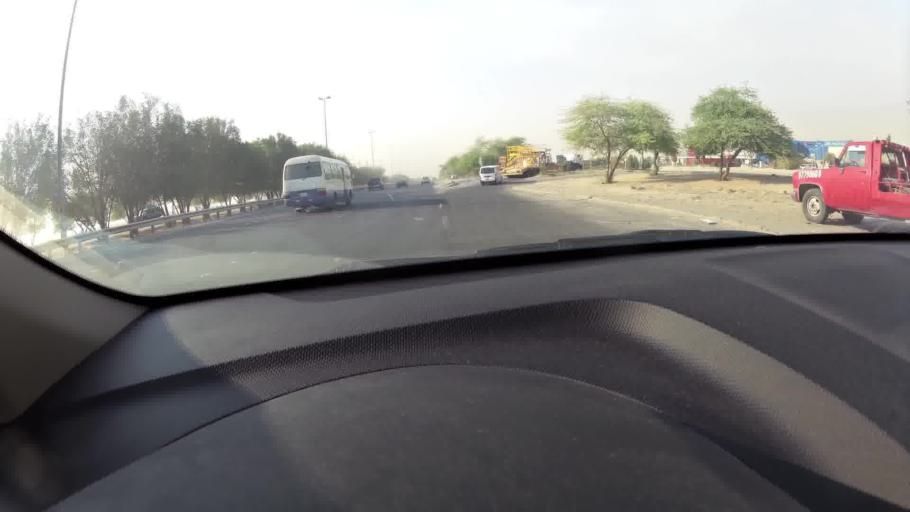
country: SA
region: Eastern Province
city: Al Khafji
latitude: 28.7327
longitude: 48.2856
